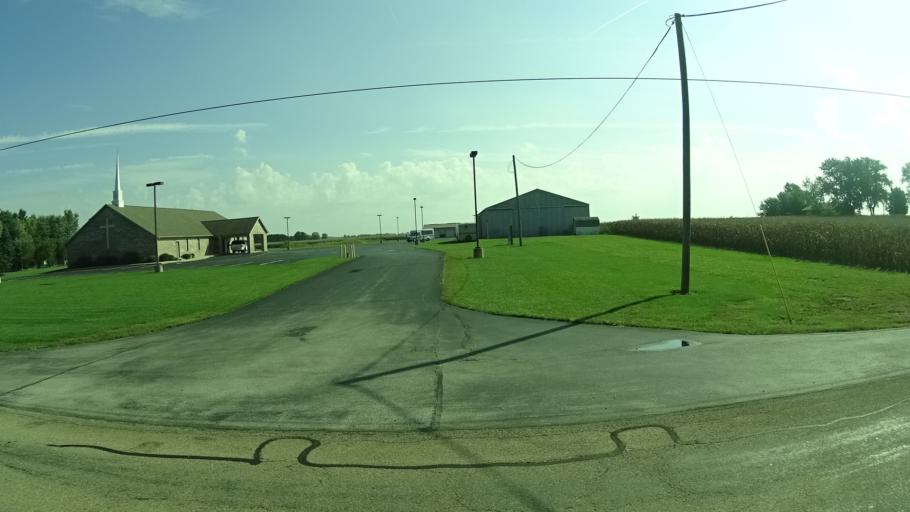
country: US
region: Indiana
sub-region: Madison County
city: Lapel
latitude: 40.0555
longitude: -85.8439
